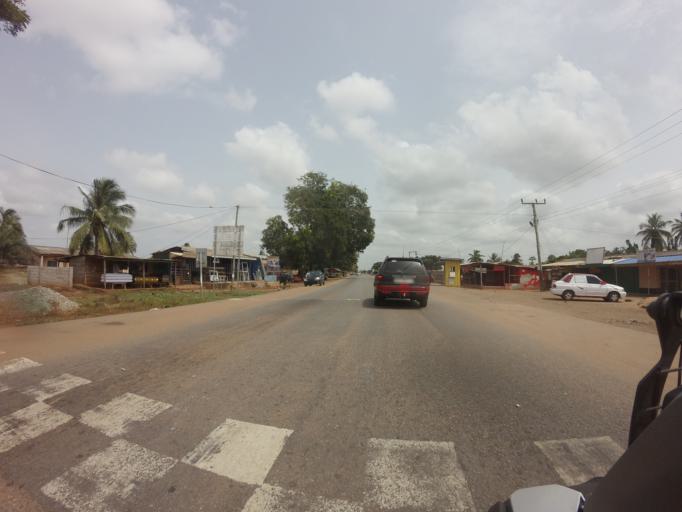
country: GH
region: Volta
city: Anloga
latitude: 5.8987
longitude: 0.5223
